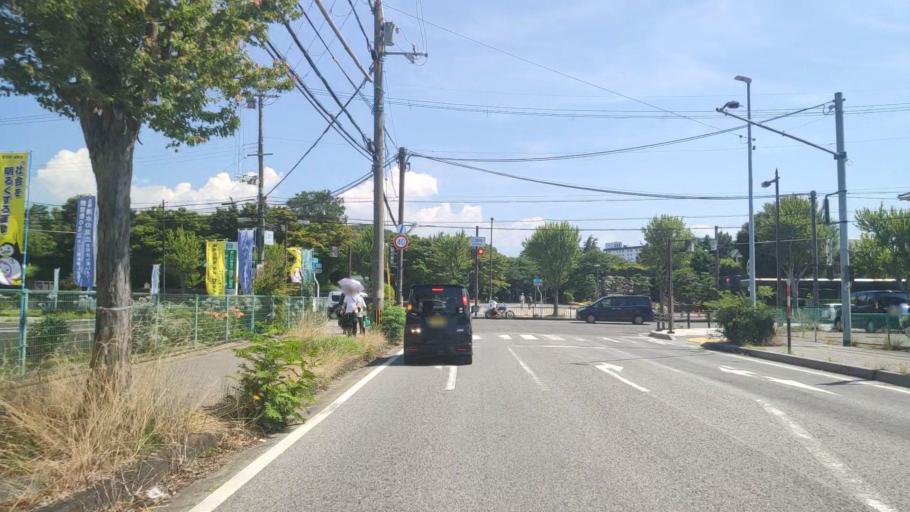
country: JP
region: Shiga Prefecture
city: Nagahama
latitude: 35.3788
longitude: 136.2617
